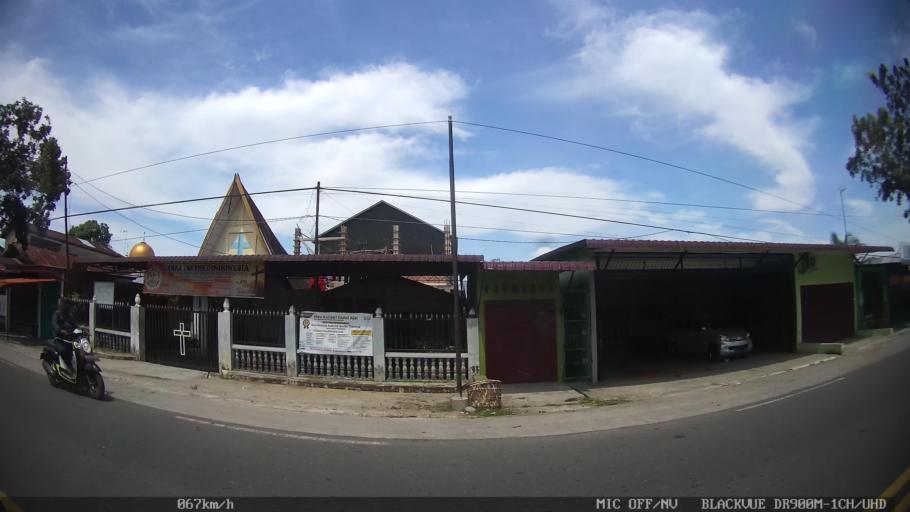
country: ID
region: North Sumatra
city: Binjai
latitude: 3.6371
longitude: 98.5104
